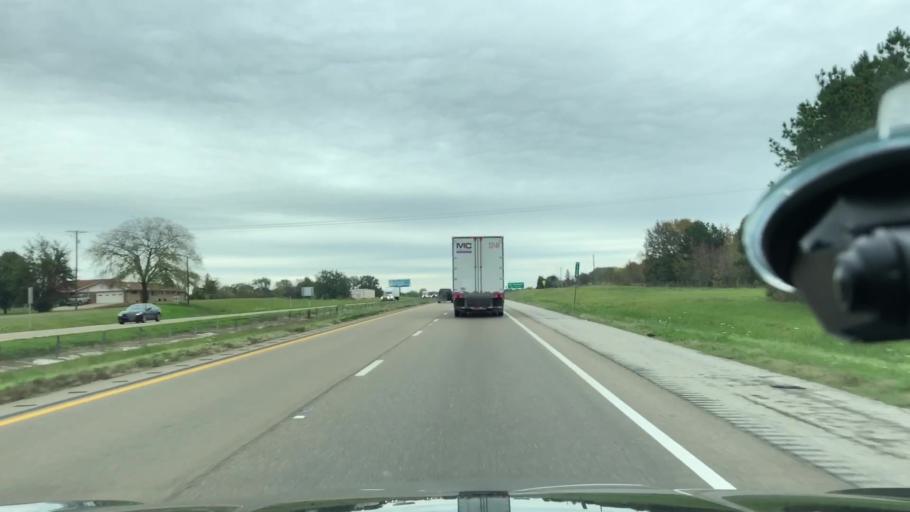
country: US
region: Texas
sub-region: Titus County
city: Mount Pleasant
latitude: 33.1612
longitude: -95.0268
